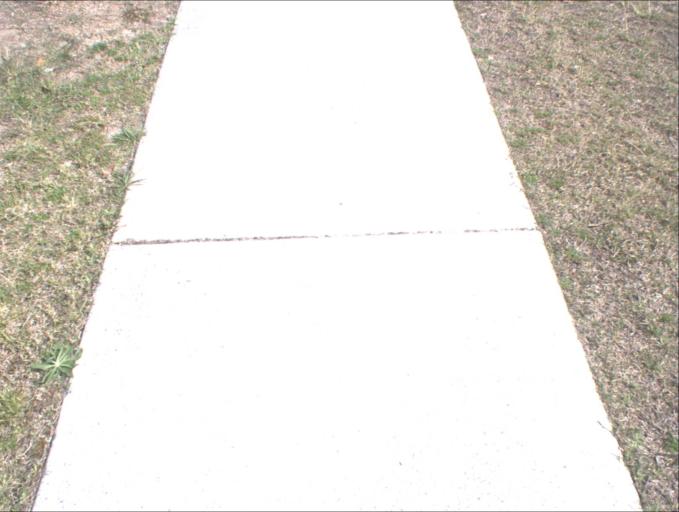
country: AU
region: Queensland
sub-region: Logan
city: Logan City
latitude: -27.6782
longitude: 153.0913
